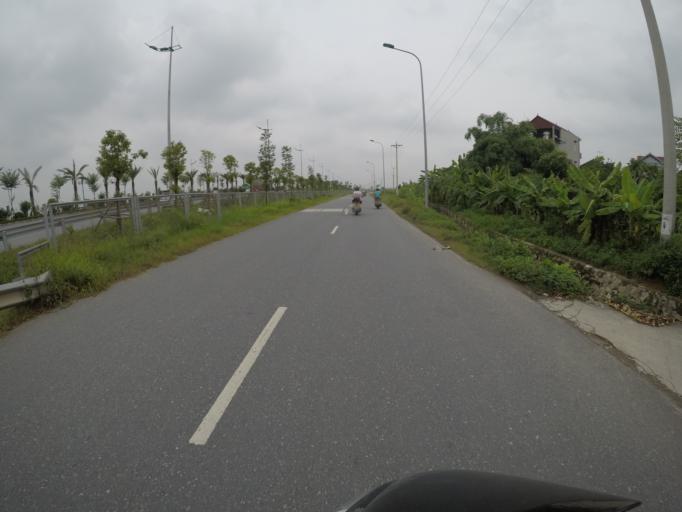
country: VN
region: Ha Noi
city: Dong Anh
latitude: 21.1788
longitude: 105.8269
